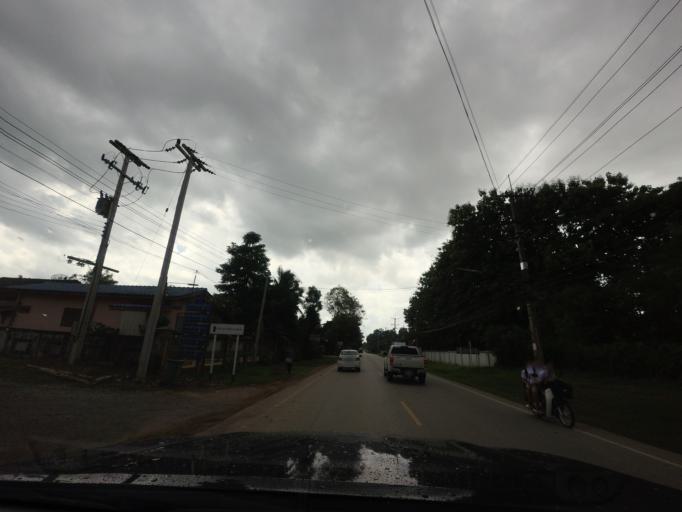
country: LA
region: Vientiane
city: Muang Sanakham
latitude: 17.8974
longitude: 101.6732
